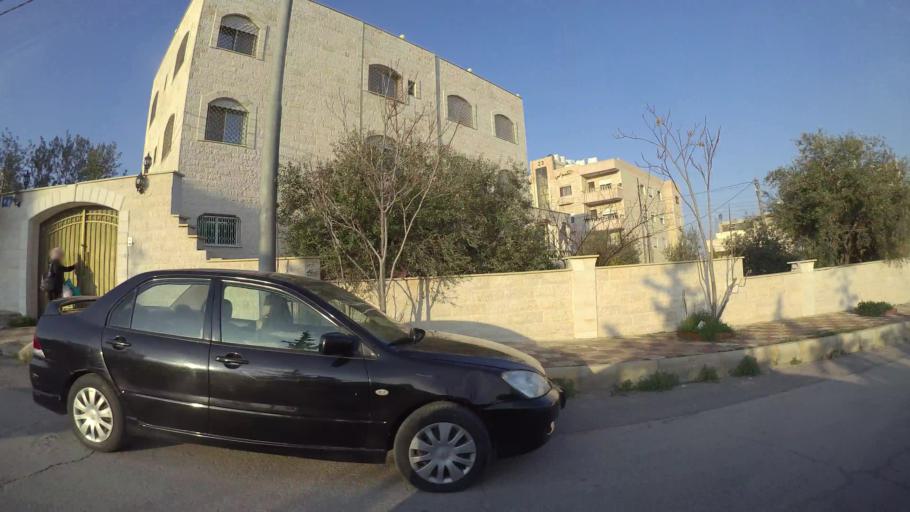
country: JO
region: Amman
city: Amman
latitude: 31.9845
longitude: 35.9712
